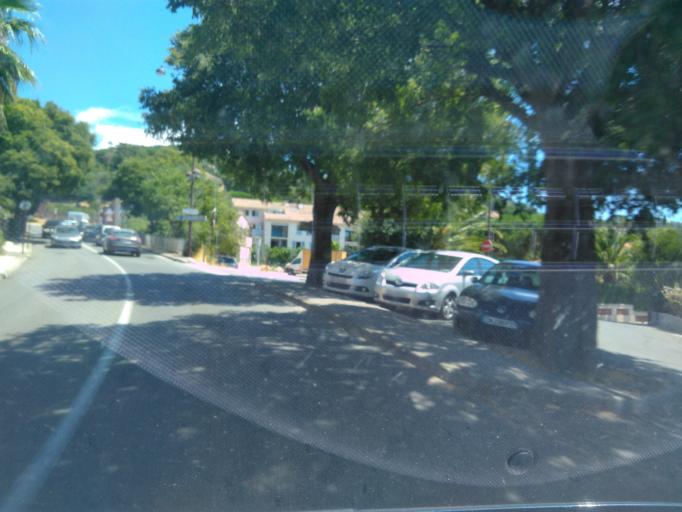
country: FR
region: Provence-Alpes-Cote d'Azur
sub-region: Departement du Var
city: La Croix-Valmer
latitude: 43.2059
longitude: 6.5673
